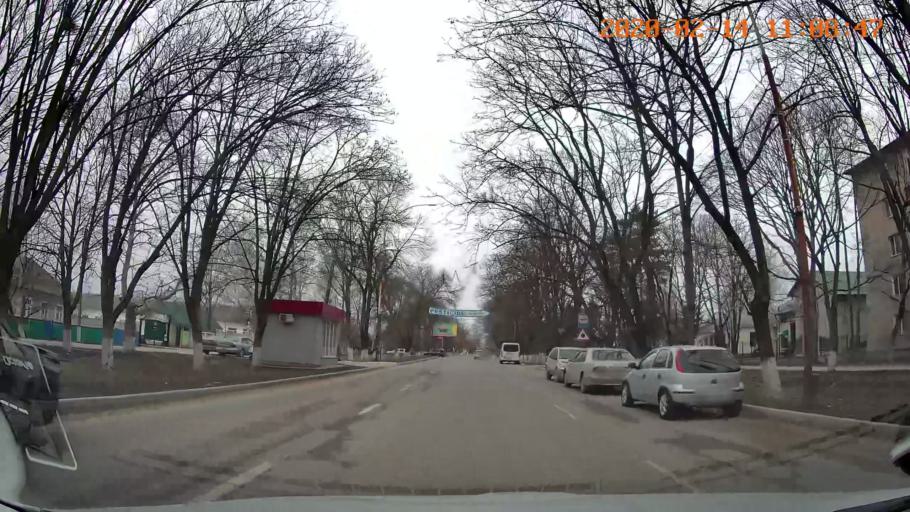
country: MD
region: Raionul Edinet
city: Edinet
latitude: 48.1741
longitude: 27.2990
